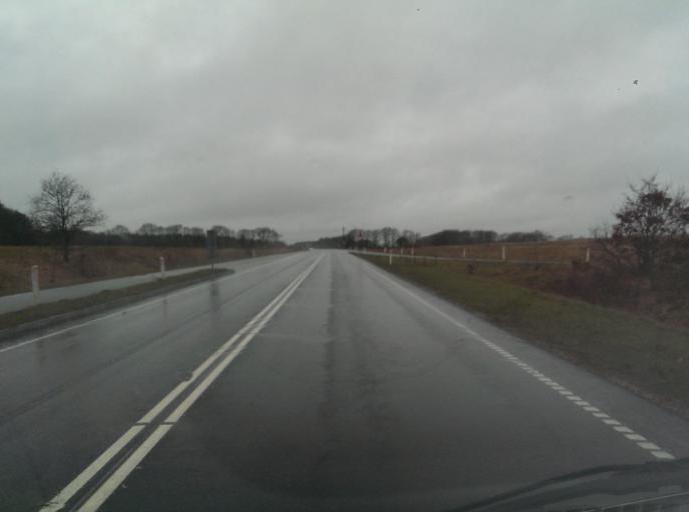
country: DK
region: South Denmark
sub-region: Varde Kommune
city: Varde
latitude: 55.6407
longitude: 8.5134
